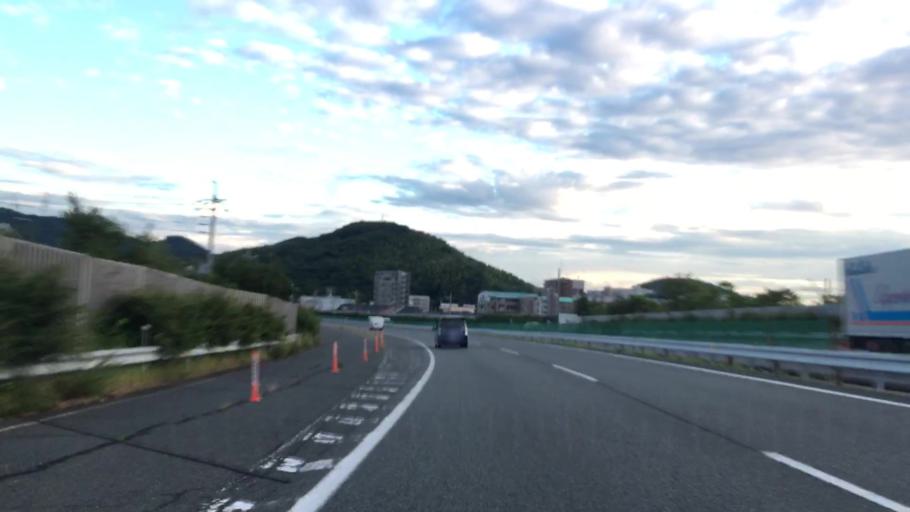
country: JP
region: Yamaguchi
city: Shimonoseki
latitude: 34.0136
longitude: 130.9557
